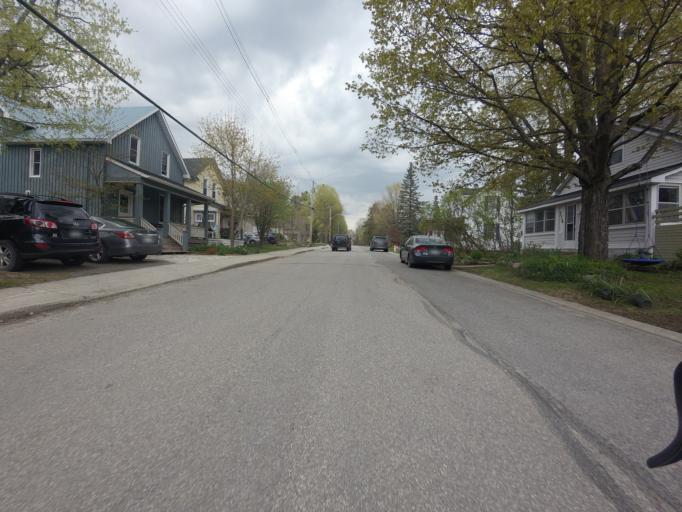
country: CA
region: Ontario
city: Carleton Place
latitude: 45.2255
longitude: -76.2034
